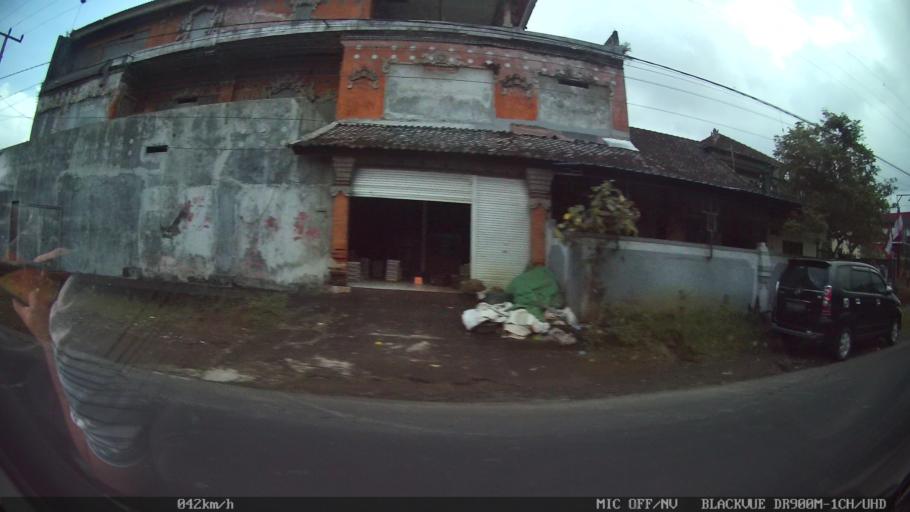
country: ID
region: Bali
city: Pohgending Kawan
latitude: -8.4546
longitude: 115.1386
